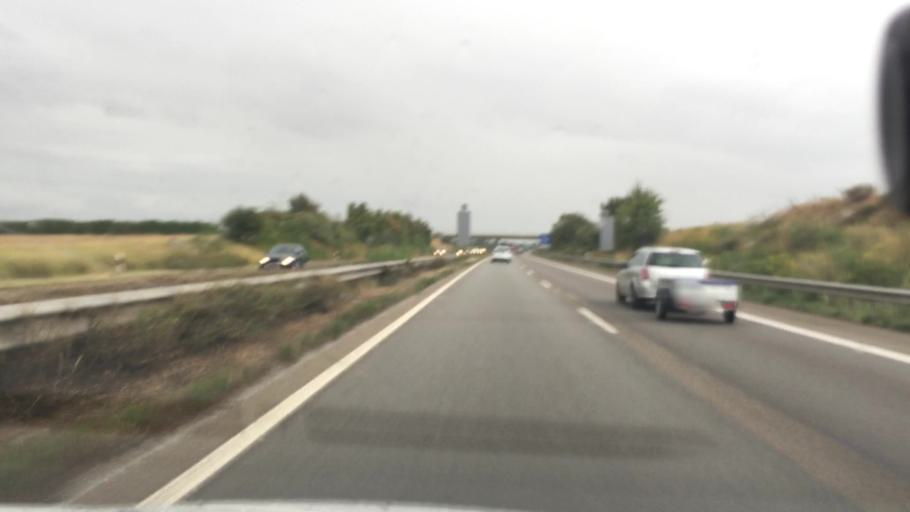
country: DE
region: Rheinland-Pfalz
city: Venningen
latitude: 49.2795
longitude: 8.1532
